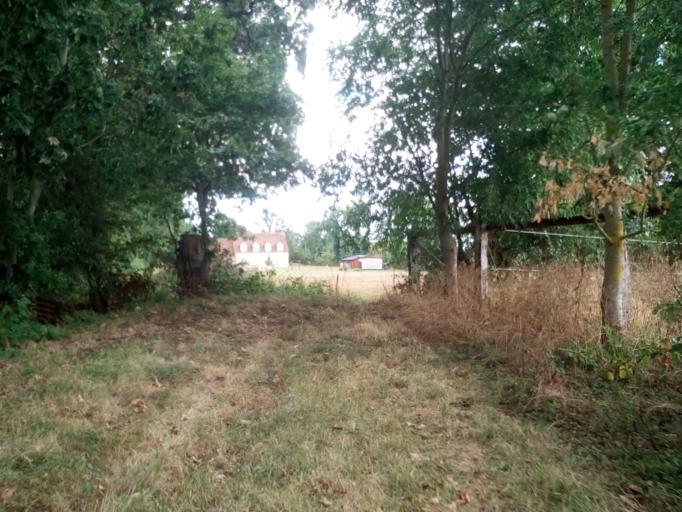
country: FR
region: Lower Normandy
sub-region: Departement du Calvados
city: Troarn
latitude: 49.1586
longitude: -0.1745
